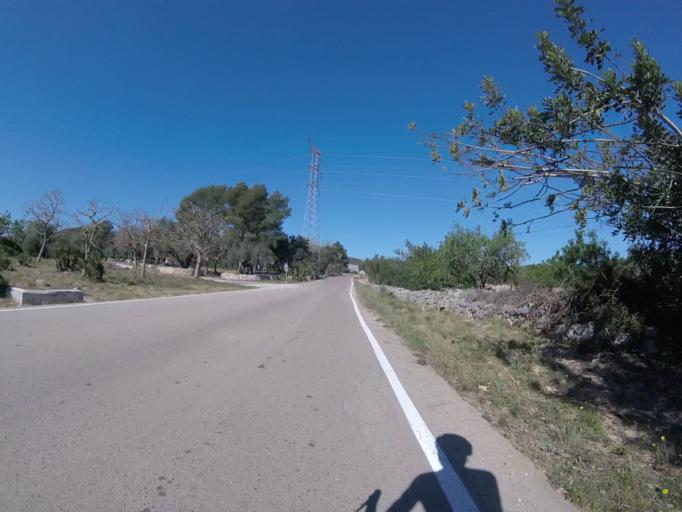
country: ES
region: Valencia
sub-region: Provincia de Castello
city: Santa Magdalena de Pulpis
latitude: 40.3607
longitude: 0.2840
